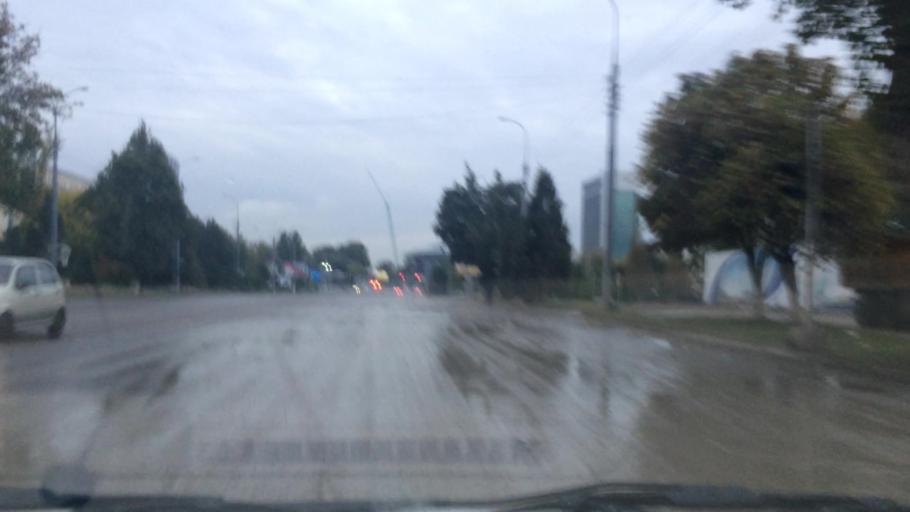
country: UZ
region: Toshkent Shahri
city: Tashkent
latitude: 41.3145
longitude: 69.2537
